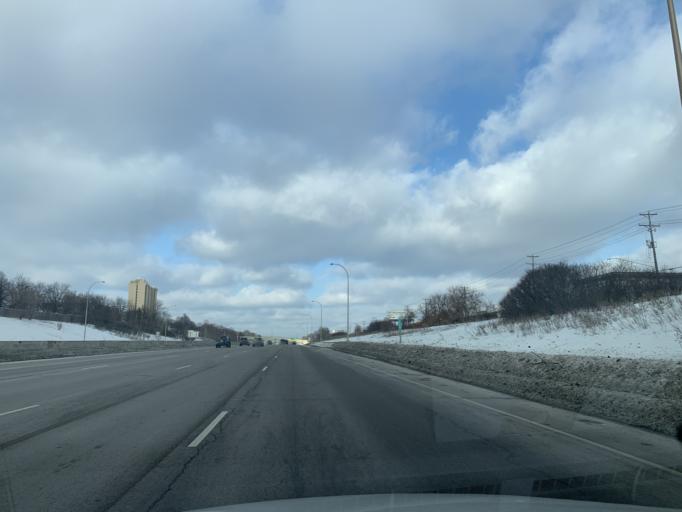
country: US
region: Minnesota
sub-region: Hennepin County
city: Minneapolis
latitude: 45.0077
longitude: -93.2824
